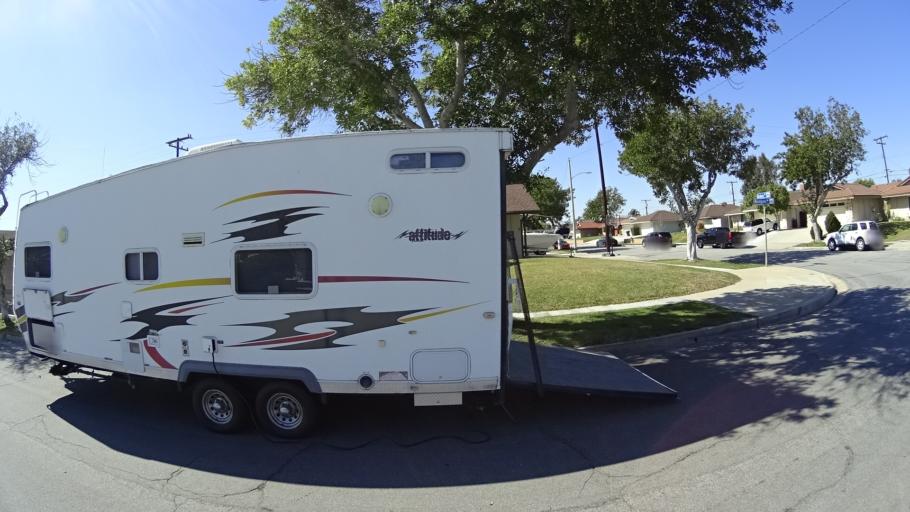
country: US
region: California
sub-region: Orange County
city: Placentia
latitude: 33.8338
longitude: -117.8677
